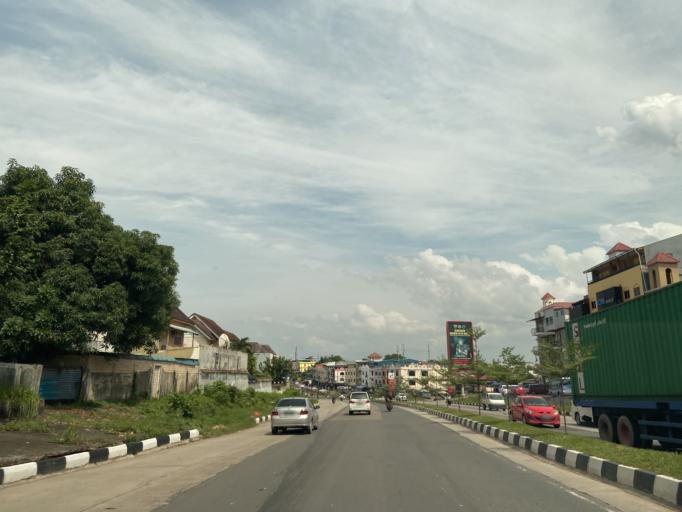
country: SG
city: Singapore
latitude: 1.1240
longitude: 104.0324
